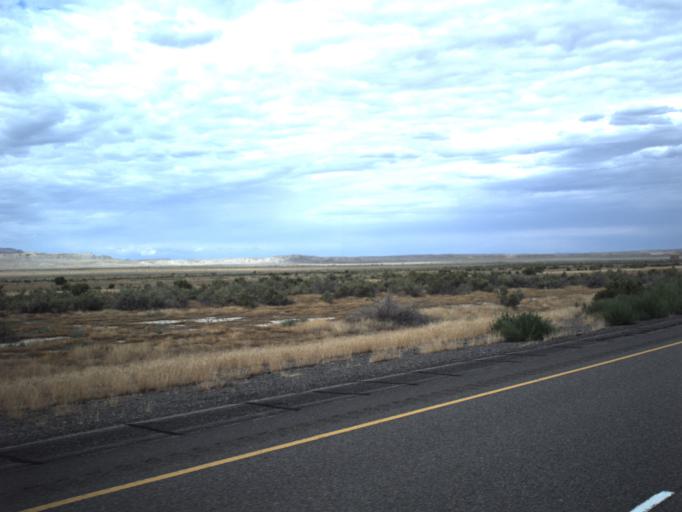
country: US
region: Utah
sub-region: Grand County
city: Moab
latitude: 38.9418
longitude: -109.5961
